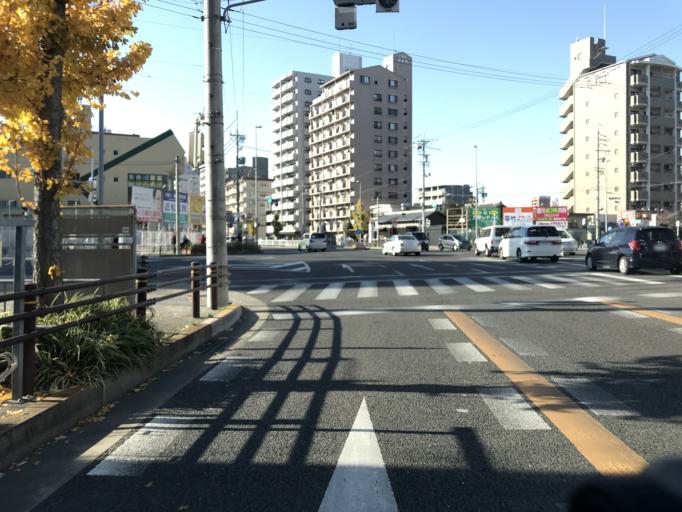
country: JP
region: Aichi
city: Nagoya-shi
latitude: 35.1957
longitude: 136.9301
